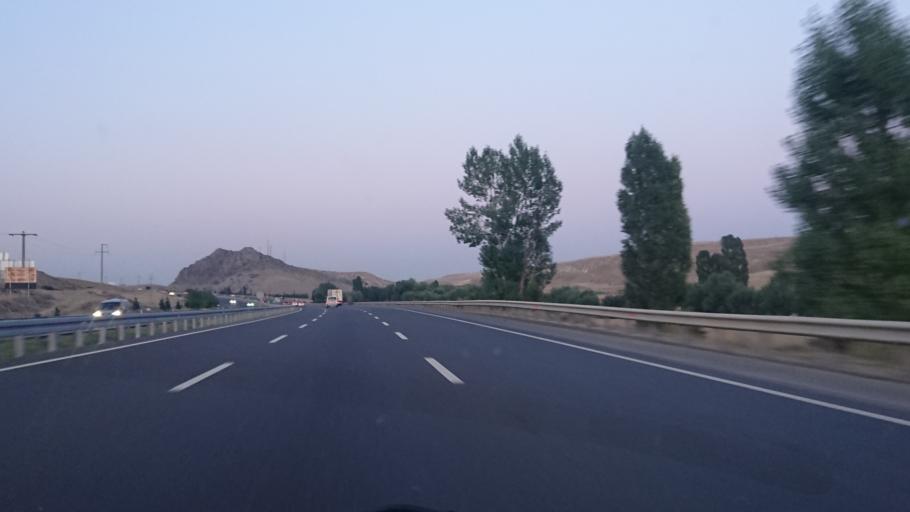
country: TR
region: Ankara
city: Temelli
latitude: 39.7638
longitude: 32.4759
